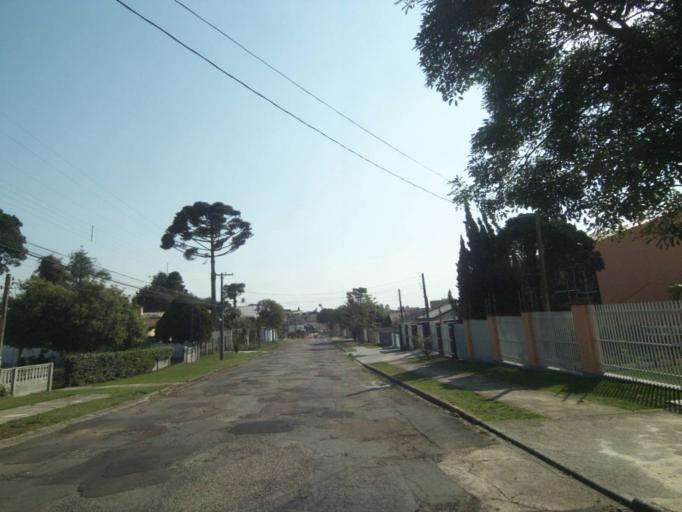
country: BR
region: Parana
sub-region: Sao Jose Dos Pinhais
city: Sao Jose dos Pinhais
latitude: -25.5074
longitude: -49.2574
